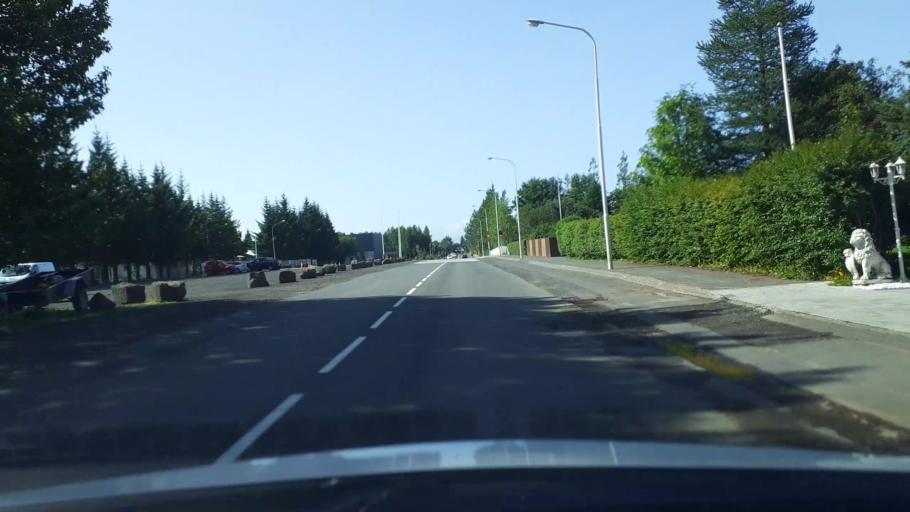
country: IS
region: South
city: Selfoss
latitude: 63.9338
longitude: -20.9909
